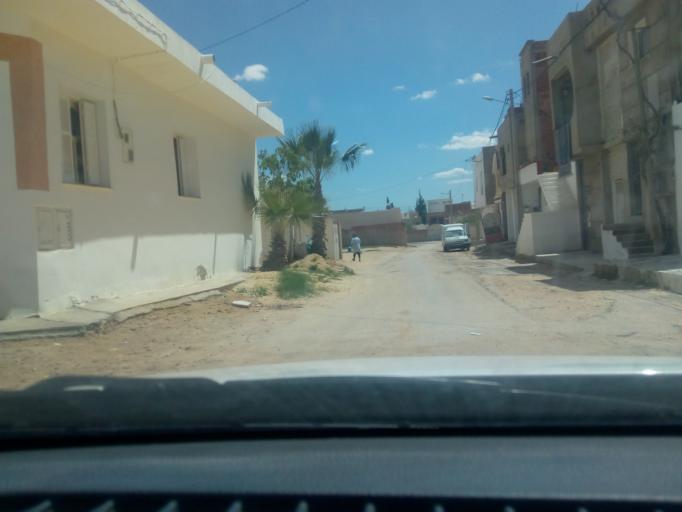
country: TN
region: Safaqis
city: Sfax
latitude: 34.7398
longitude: 10.5246
